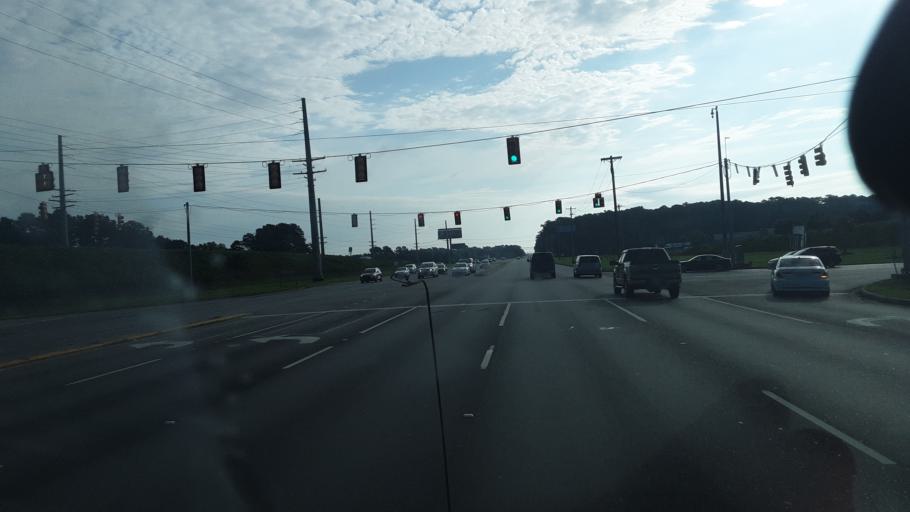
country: US
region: South Carolina
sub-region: Horry County
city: North Myrtle Beach
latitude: 33.7878
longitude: -78.7743
